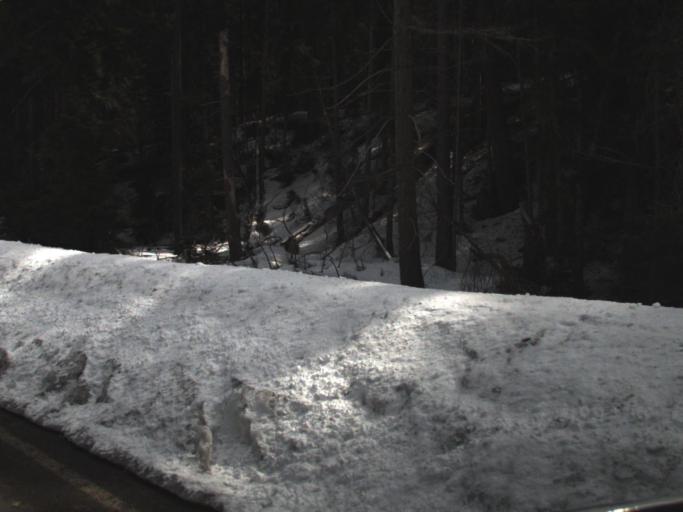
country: US
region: Washington
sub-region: Kittitas County
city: Cle Elum
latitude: 46.9646
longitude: -121.2653
